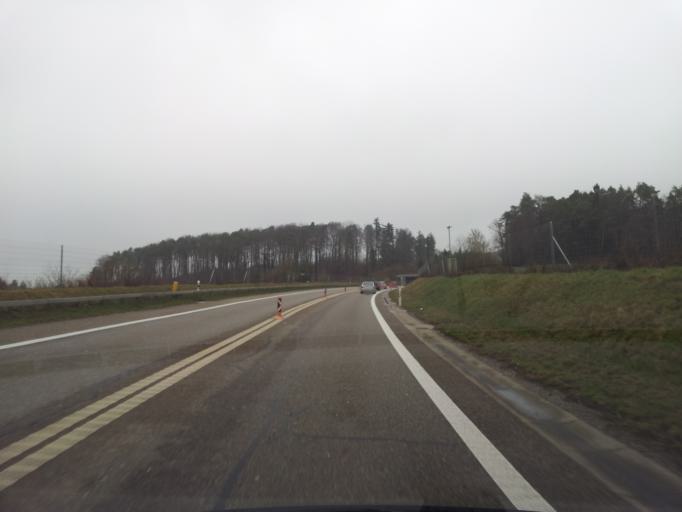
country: CH
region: Zurich
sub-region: Bezirk Andelfingen
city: Henggart
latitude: 47.5533
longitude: 8.6872
